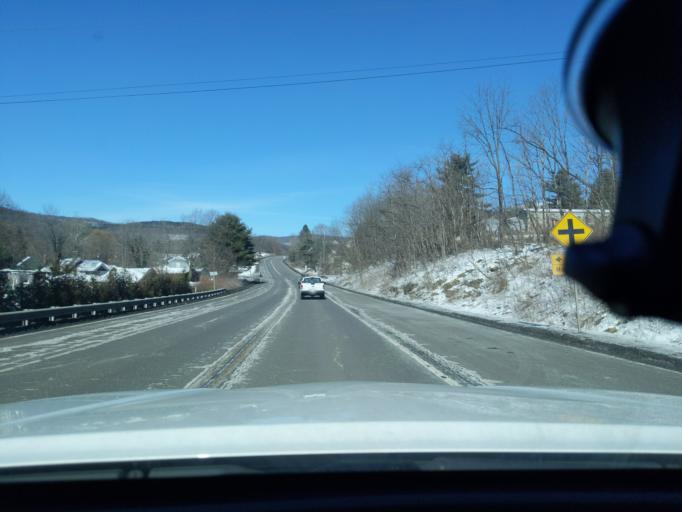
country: US
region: Maryland
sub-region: Allegany County
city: Westernport
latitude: 39.5215
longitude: -79.0181
